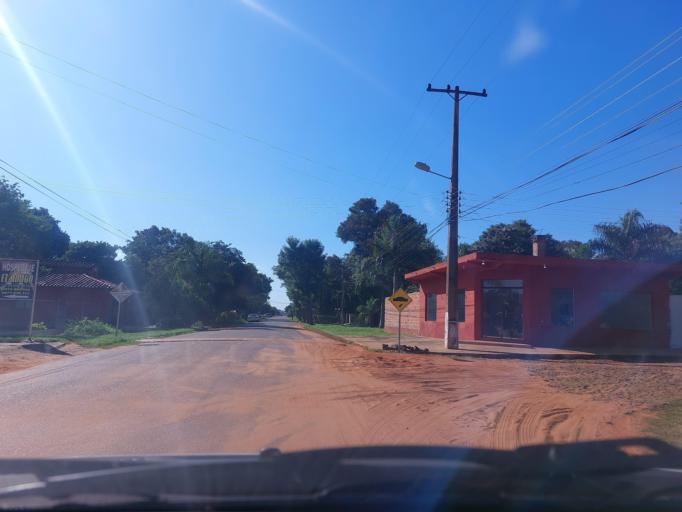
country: PY
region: San Pedro
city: Guayaybi
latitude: -24.5309
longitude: -56.4040
